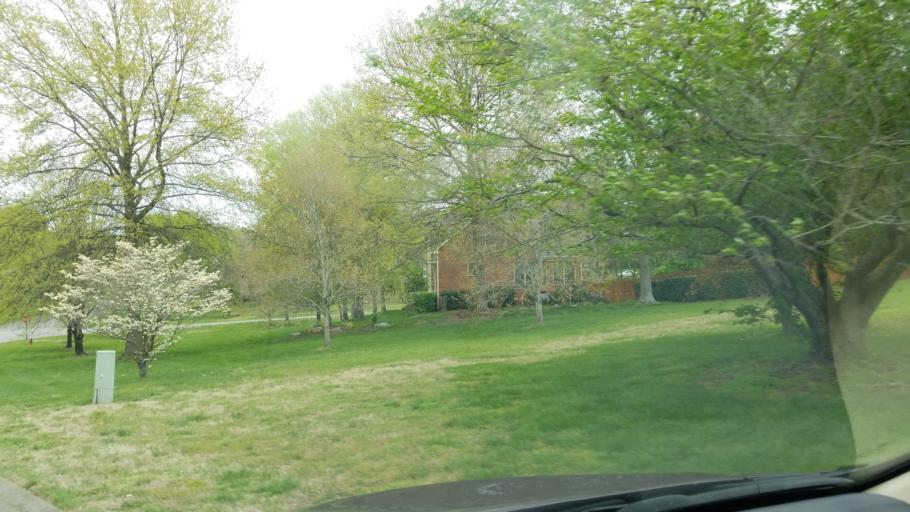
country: US
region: Tennessee
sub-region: Williamson County
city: Brentwood Estates
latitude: 36.0005
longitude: -86.7742
